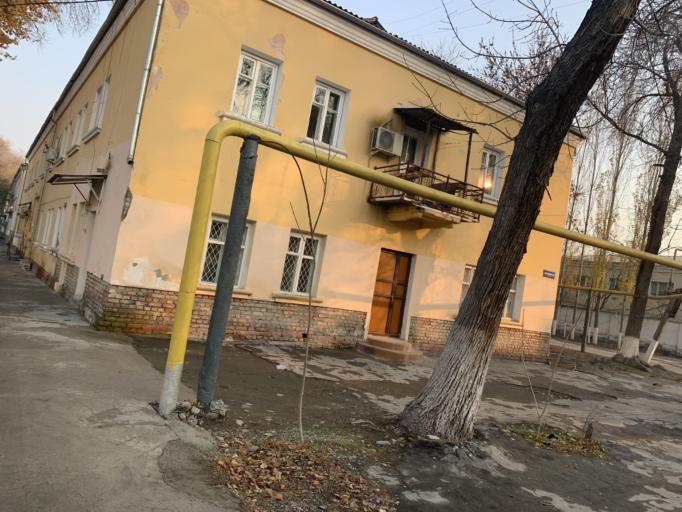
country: UZ
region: Fergana
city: Qo`qon
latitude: 40.5235
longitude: 70.9384
